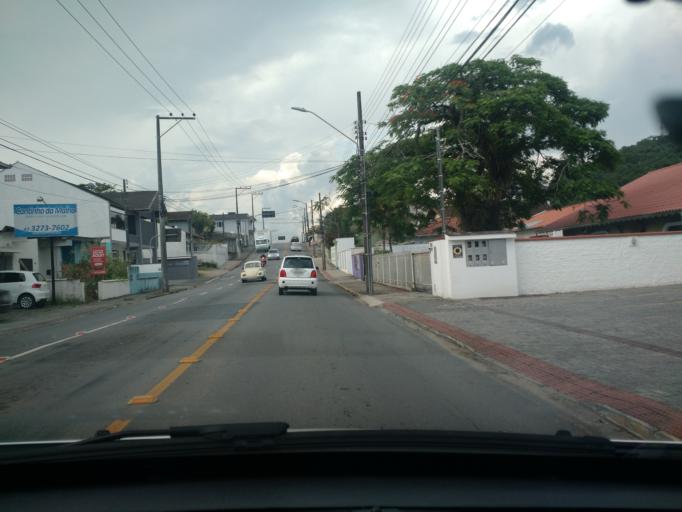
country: BR
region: Santa Catarina
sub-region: Jaragua Do Sul
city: Jaragua do Sul
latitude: -26.4950
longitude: -49.0899
